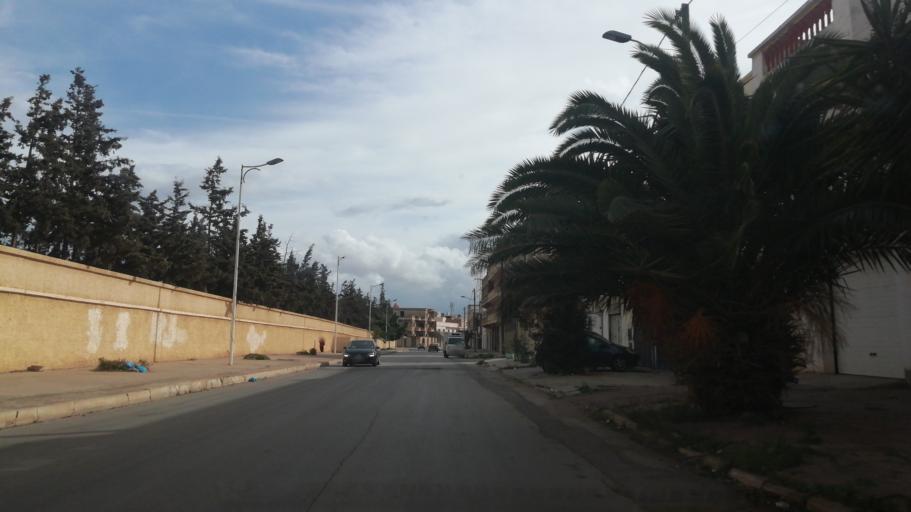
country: DZ
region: Oran
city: Es Senia
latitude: 35.6636
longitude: -0.6393
